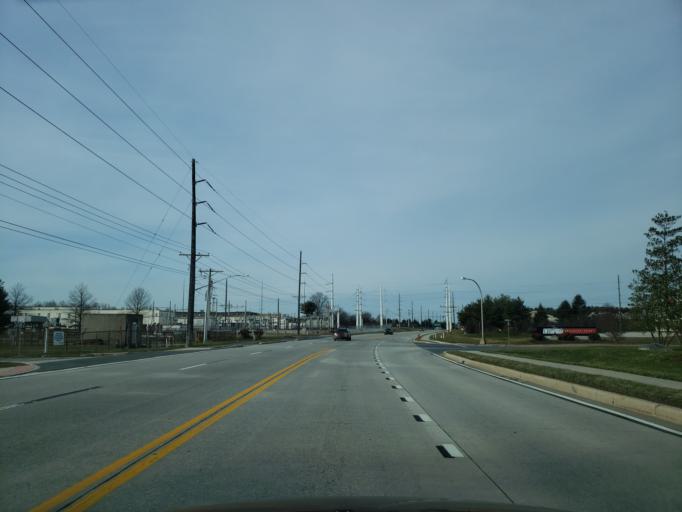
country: US
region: Delaware
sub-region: Kent County
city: Dover
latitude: 39.1516
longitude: -75.5465
